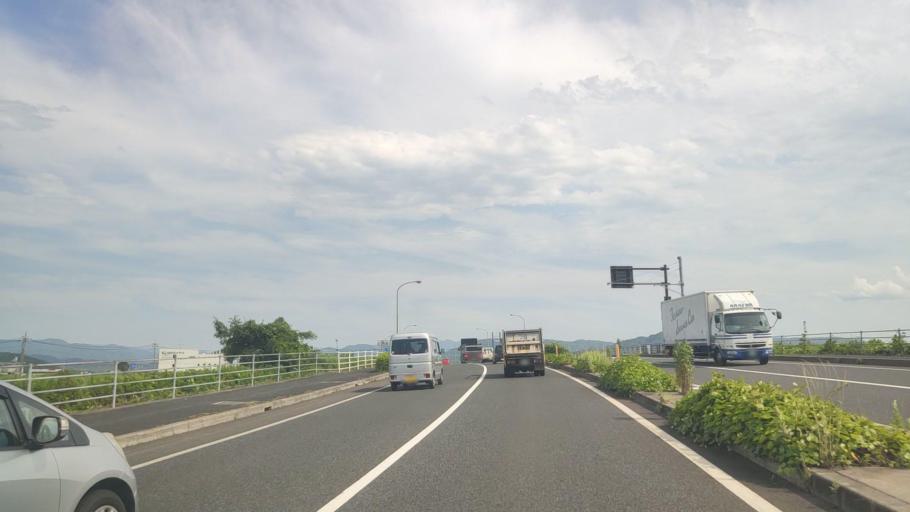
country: JP
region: Tottori
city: Tottori
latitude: 35.4819
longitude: 134.2062
